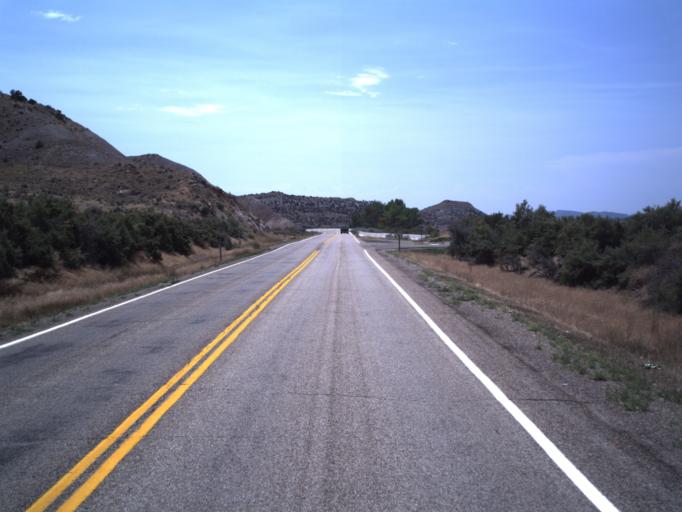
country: US
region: Utah
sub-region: Uintah County
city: Vernal
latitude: 40.5305
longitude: -109.5221
